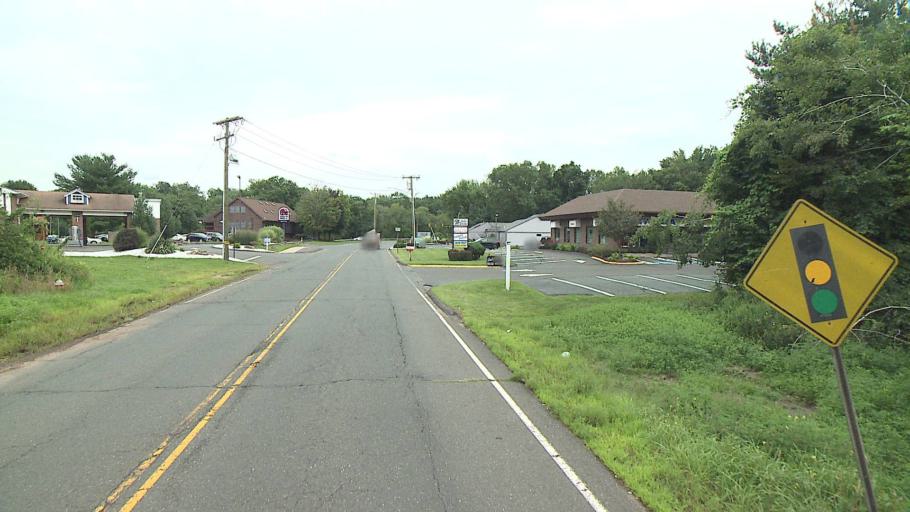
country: US
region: Connecticut
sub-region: Middlesex County
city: Cromwell
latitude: 41.6002
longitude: -72.6785
